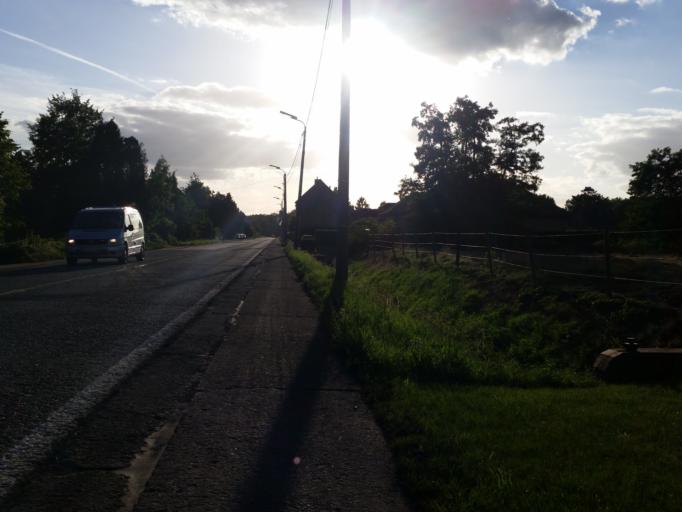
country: BE
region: Flanders
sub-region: Provincie Antwerpen
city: Duffel
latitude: 51.0702
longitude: 4.4846
